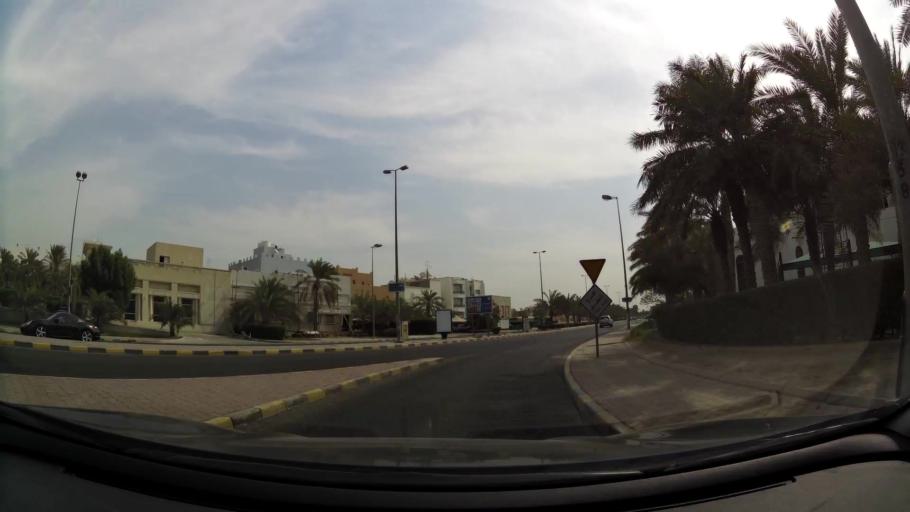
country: KW
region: Al Asimah
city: Ash Shamiyah
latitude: 29.3443
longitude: 47.9795
